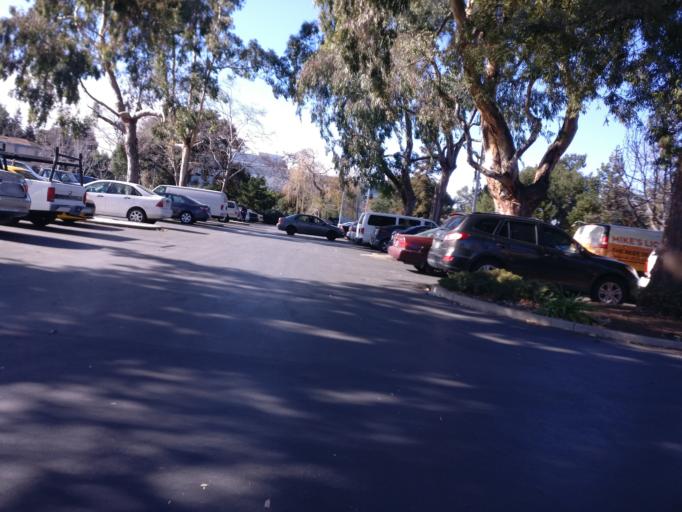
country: US
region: California
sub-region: Alameda County
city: Emeryville
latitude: 37.8390
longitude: -122.2586
